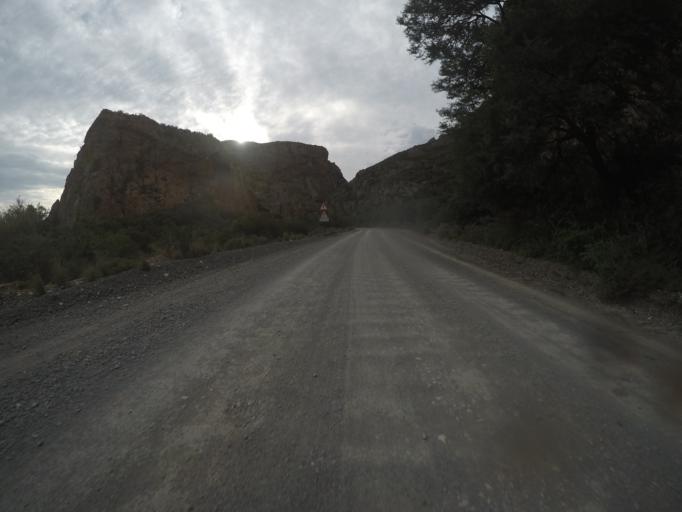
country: ZA
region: Eastern Cape
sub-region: Cacadu District Municipality
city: Willowmore
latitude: -33.5229
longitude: 23.6534
